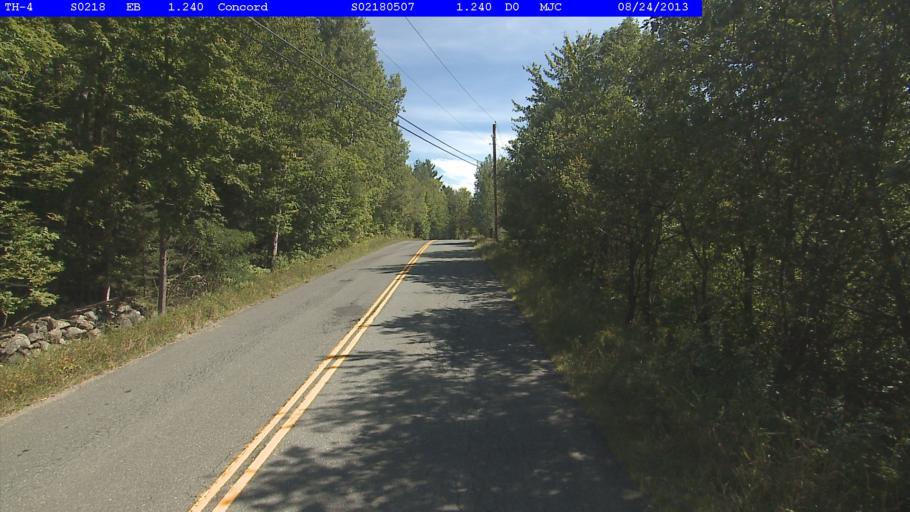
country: US
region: New Hampshire
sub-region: Grafton County
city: Littleton
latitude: 44.4483
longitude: -71.7666
